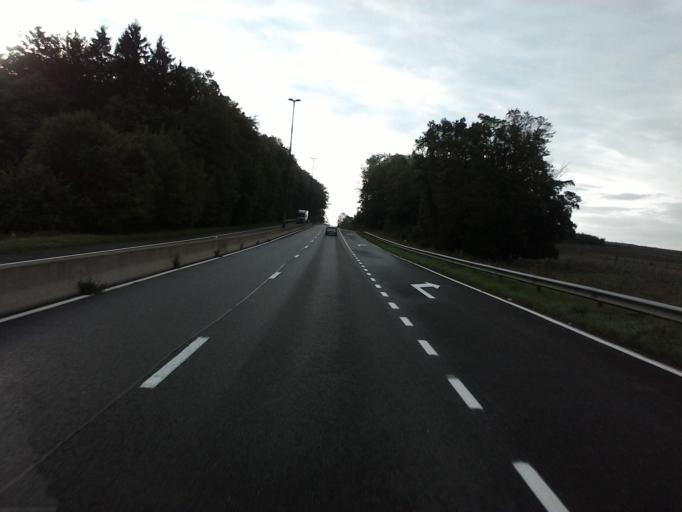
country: BE
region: Wallonia
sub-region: Province du Luxembourg
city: Attert
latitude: 49.7341
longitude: 5.7899
